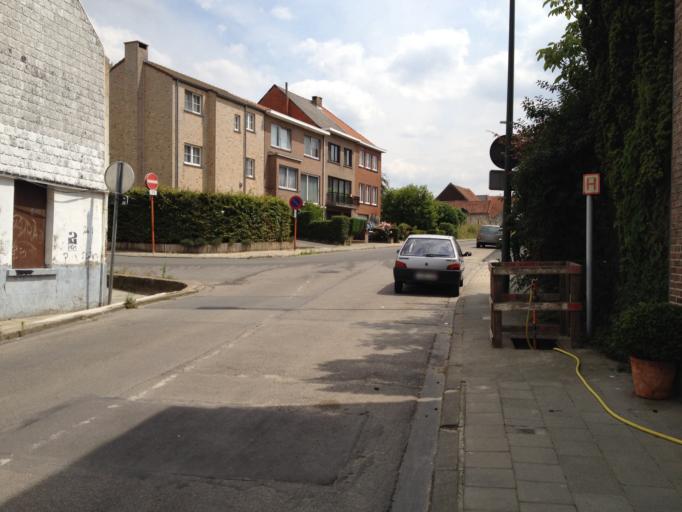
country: BE
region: Flanders
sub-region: Provincie Vlaams-Brabant
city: Wemmel
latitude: 50.9056
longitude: 4.3108
